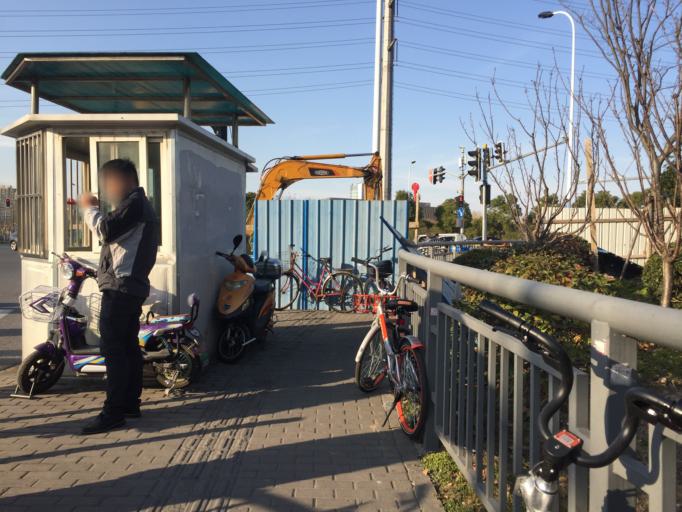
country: CN
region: Shanghai Shi
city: Huamu
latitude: 31.1893
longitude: 121.5362
